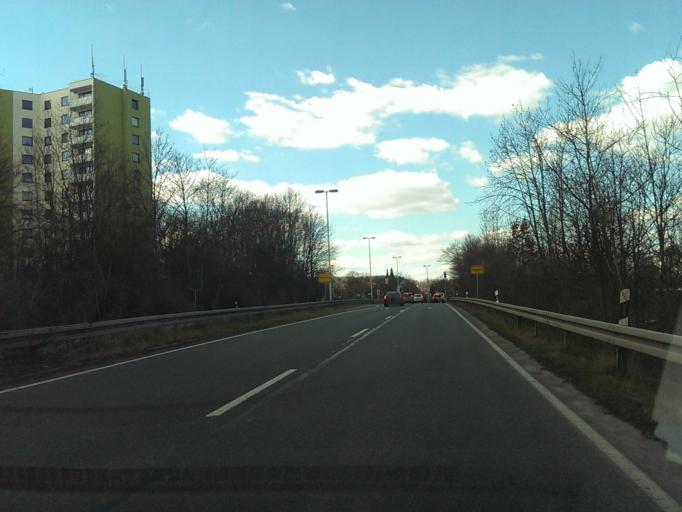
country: DE
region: Lower Saxony
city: Hildesheim
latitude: 52.1359
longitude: 9.9445
